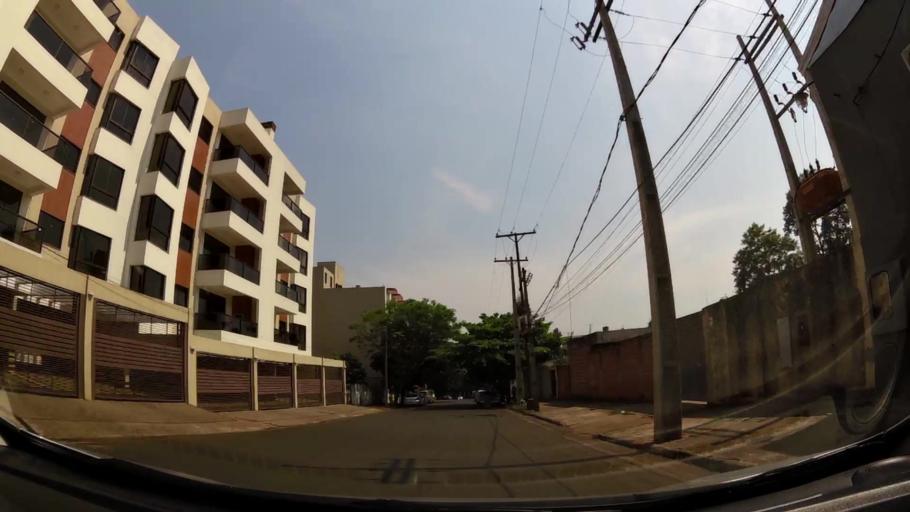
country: PY
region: Alto Parana
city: Presidente Franco
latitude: -25.5211
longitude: -54.6159
